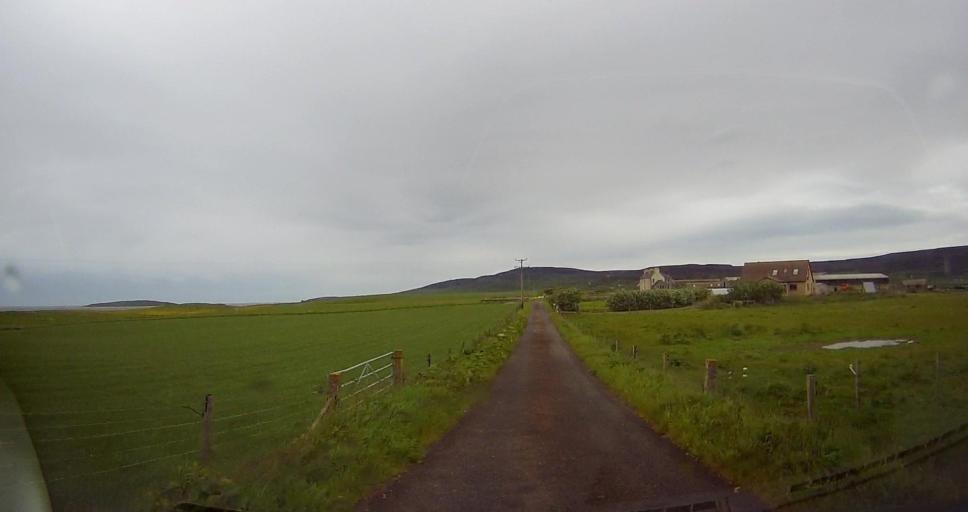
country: GB
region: Scotland
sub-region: Orkney Islands
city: Orkney
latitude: 59.1151
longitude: -3.0750
